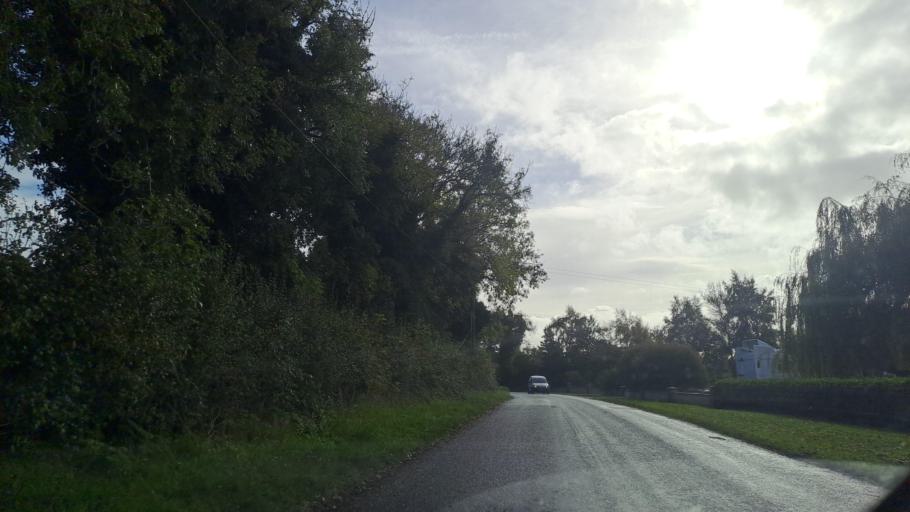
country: IE
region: Leinster
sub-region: Lu
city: Ardee
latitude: 53.8606
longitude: -6.6581
